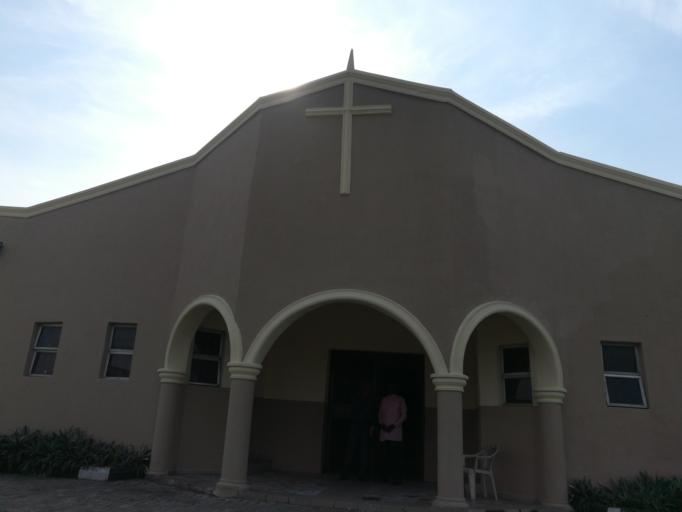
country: NG
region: Rivers
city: Okrika
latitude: 4.7375
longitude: 7.0863
